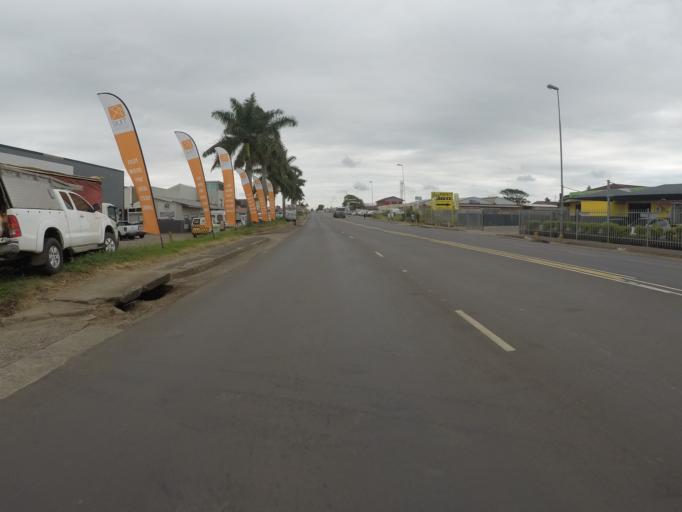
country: ZA
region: KwaZulu-Natal
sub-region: uThungulu District Municipality
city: Empangeni
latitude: -28.7767
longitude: 31.8938
